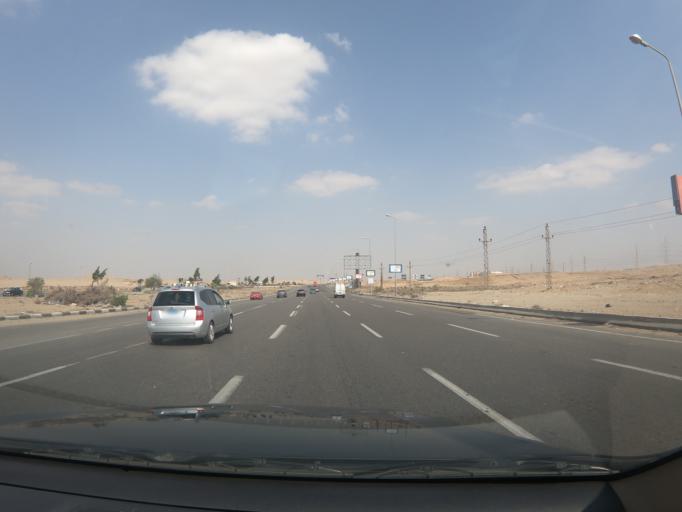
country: EG
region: Muhafazat al Qalyubiyah
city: Al Khankah
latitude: 30.0860
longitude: 31.4878
